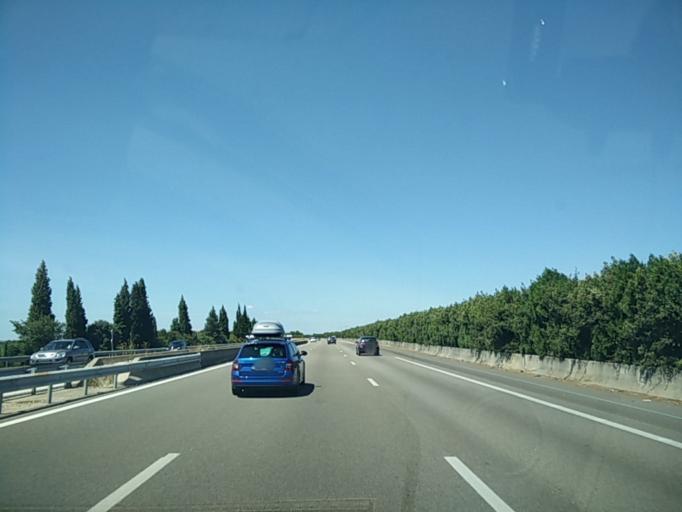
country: FR
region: Provence-Alpes-Cote d'Azur
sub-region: Departement du Vaucluse
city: Courthezon
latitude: 44.1054
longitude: 4.8570
